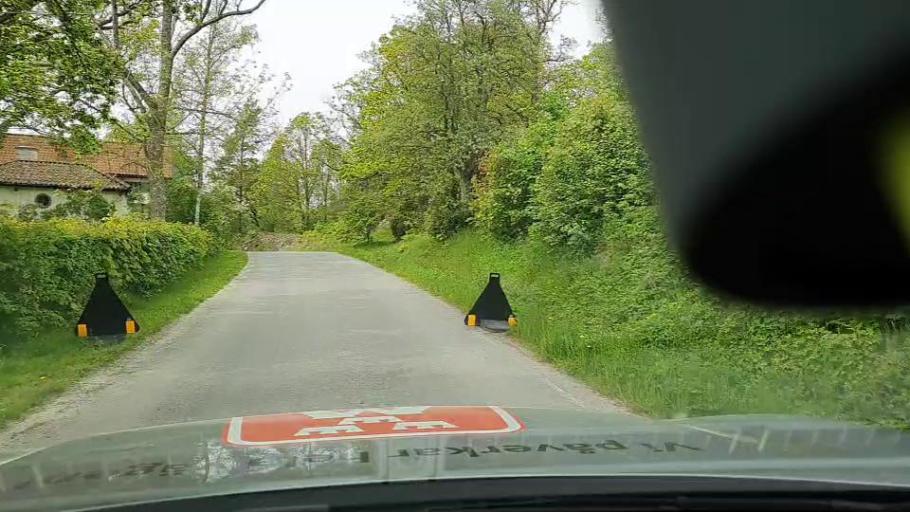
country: SE
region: Soedermanland
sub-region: Flens Kommun
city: Halleforsnas
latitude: 59.1001
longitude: 16.4843
